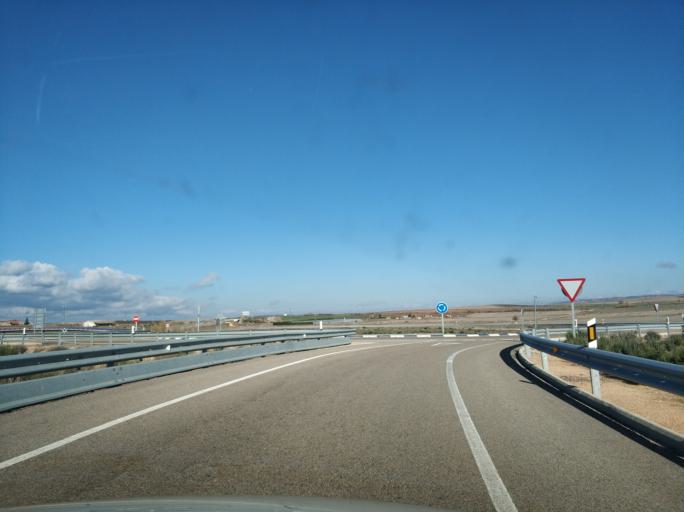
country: ES
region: Castille and Leon
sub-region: Provincia de Soria
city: Almazan
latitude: 41.4703
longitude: -2.5236
